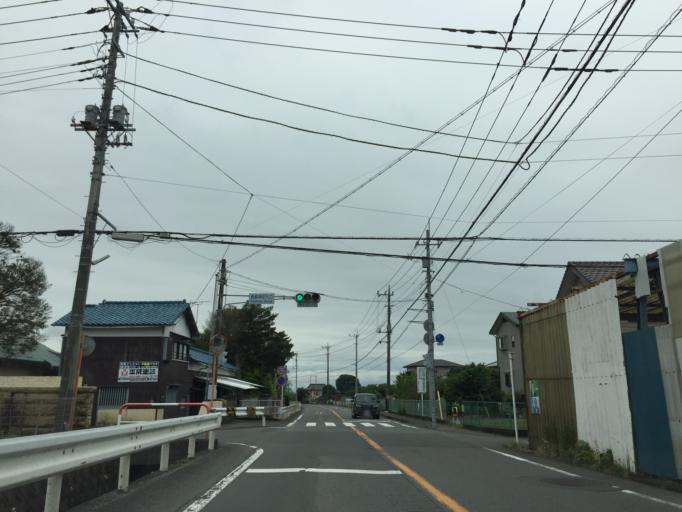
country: JP
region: Shizuoka
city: Mishima
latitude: 35.1831
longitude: 138.9201
